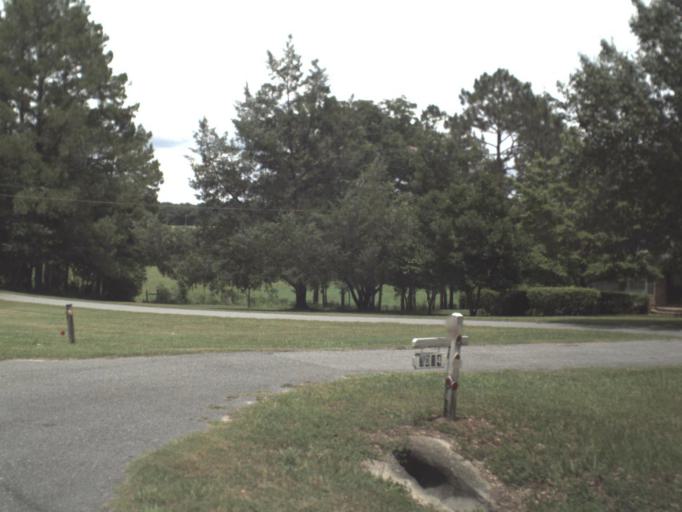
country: US
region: Florida
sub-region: Madison County
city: Madison
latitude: 30.4981
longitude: -83.3822
